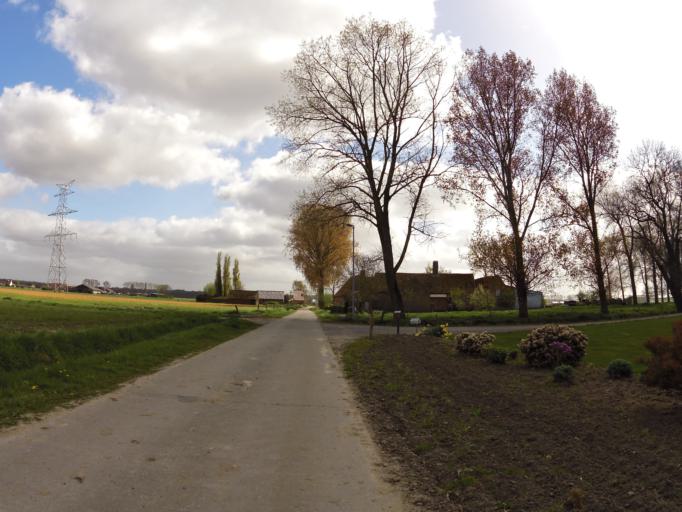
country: BE
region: Flanders
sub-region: Provincie West-Vlaanderen
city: Jabbeke
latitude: 51.1979
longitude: 3.1183
